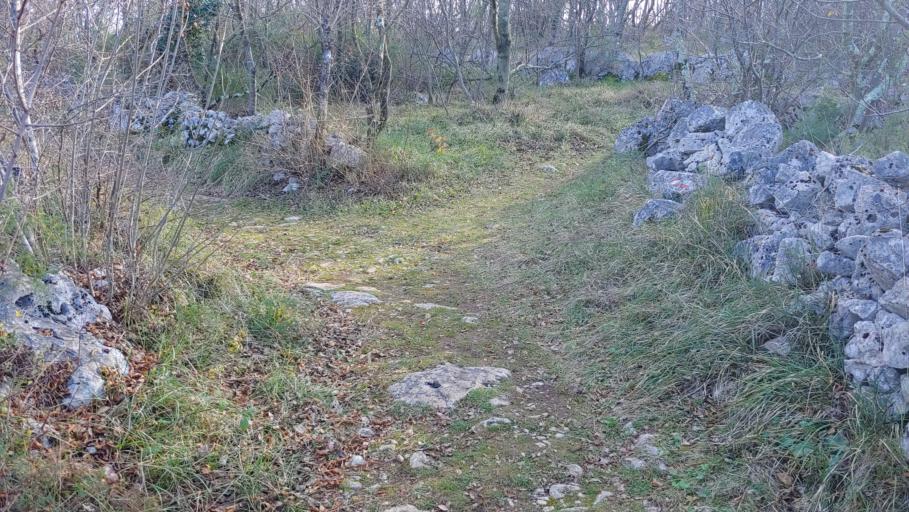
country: IT
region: Friuli Venezia Giulia
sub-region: Provincia di Trieste
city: Aurisina
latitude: 45.7674
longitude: 13.6713
